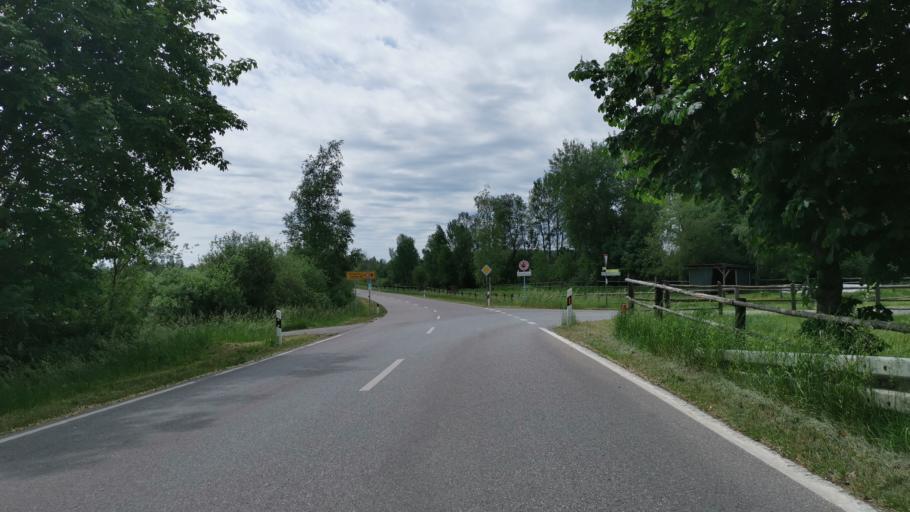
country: DE
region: Bavaria
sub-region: Upper Bavaria
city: Hattenhofen
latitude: 48.2203
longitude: 11.0993
